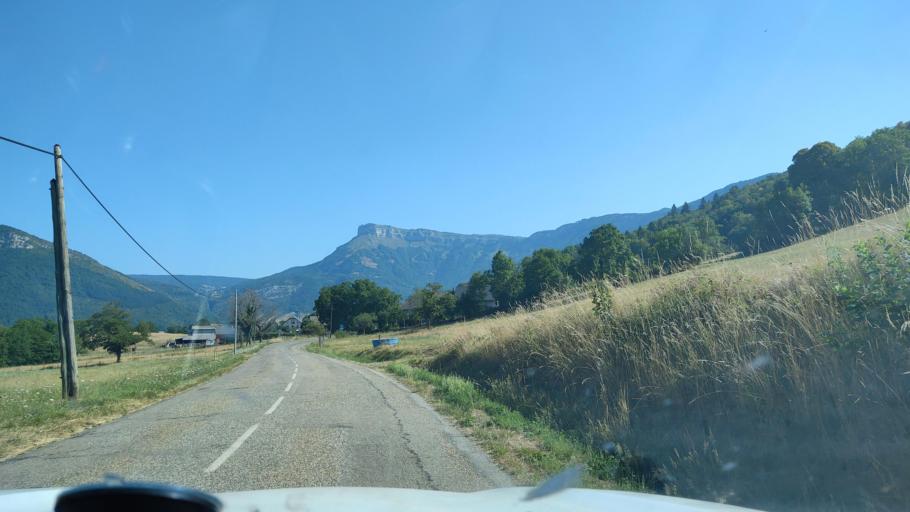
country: FR
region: Rhone-Alpes
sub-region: Departement de la Savoie
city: Barby
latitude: 45.5644
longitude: 6.0240
